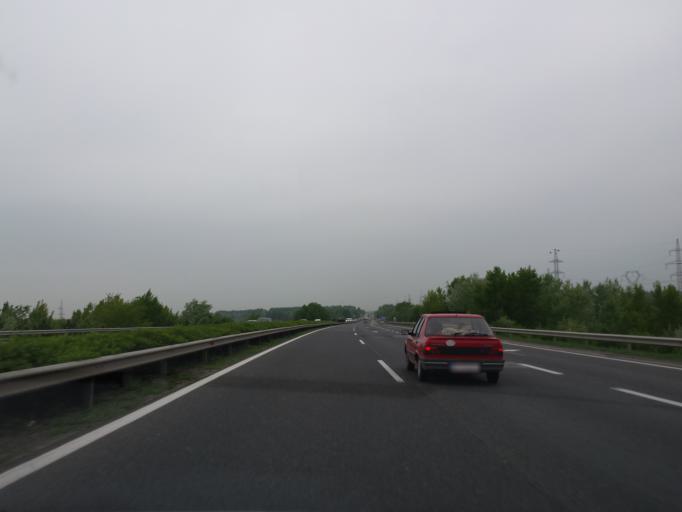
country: HU
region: Gyor-Moson-Sopron
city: Gyor
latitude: 47.6441
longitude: 17.6190
